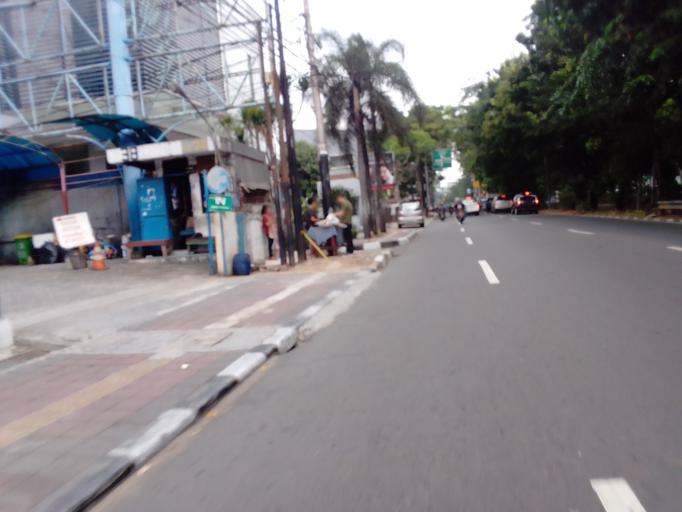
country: ID
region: Jakarta Raya
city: Jakarta
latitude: -6.1697
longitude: 106.8111
